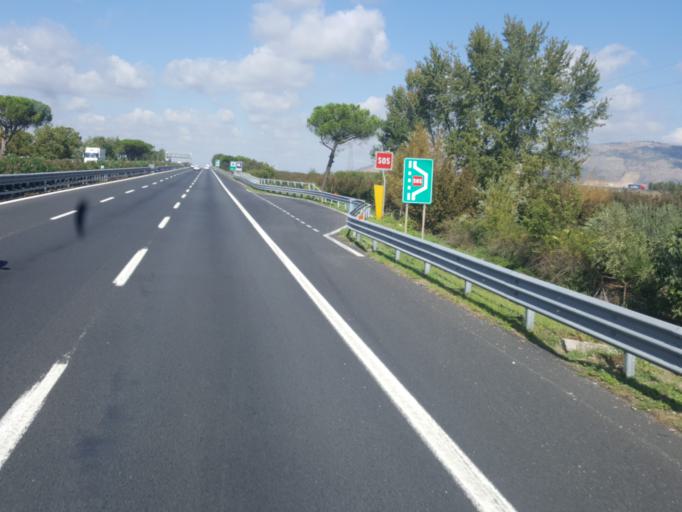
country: IT
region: Campania
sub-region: Provincia di Napoli
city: San Vitaliano
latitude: 40.9453
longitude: 14.4840
